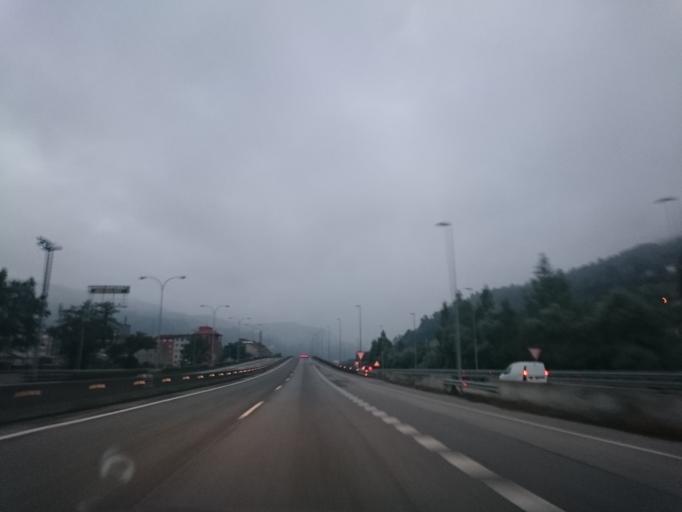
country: ES
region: Asturias
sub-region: Province of Asturias
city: Mieres
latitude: 43.2580
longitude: -5.7825
